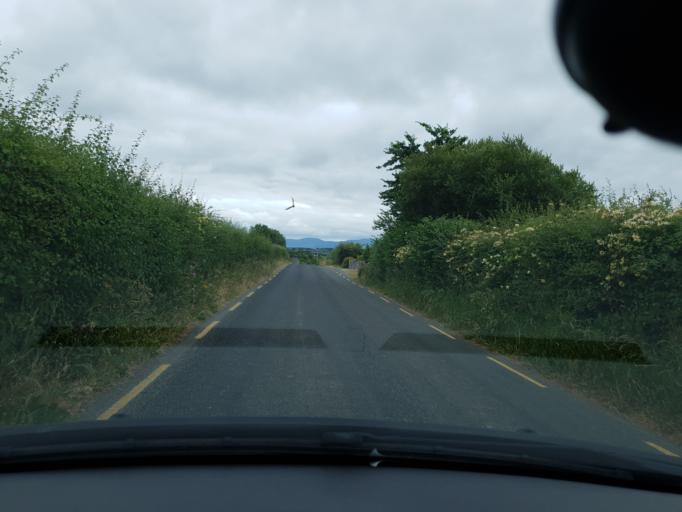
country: IE
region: Munster
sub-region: Ciarrai
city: Cill Airne
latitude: 52.1415
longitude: -9.5879
